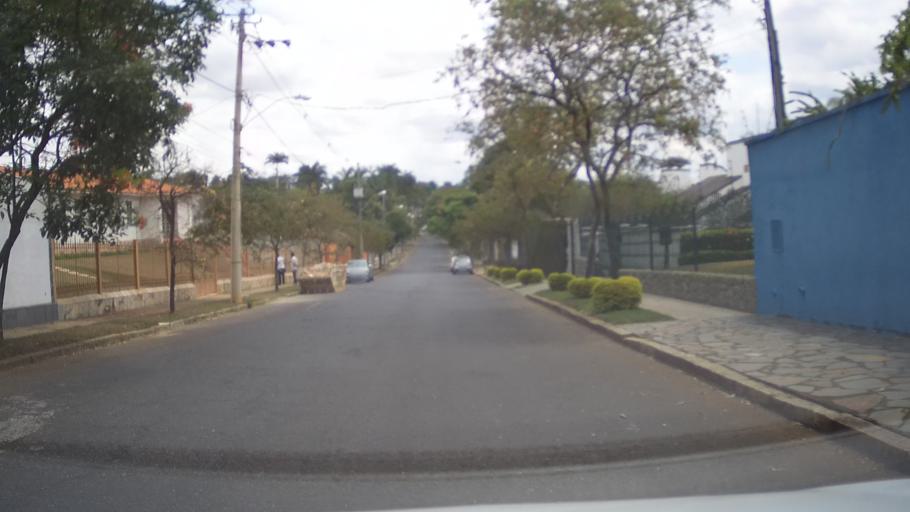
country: BR
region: Minas Gerais
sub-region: Belo Horizonte
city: Belo Horizonte
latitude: -19.8552
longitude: -43.9672
